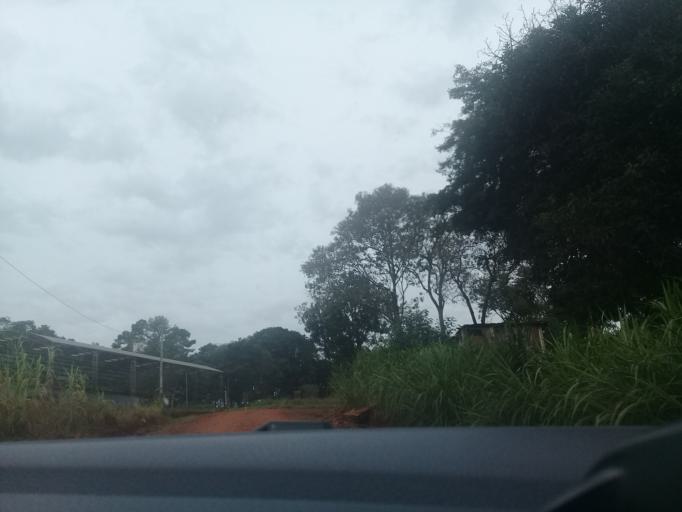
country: AR
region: Misiones
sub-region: Departamento de Obera
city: Obera
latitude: -27.4776
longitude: -55.1519
